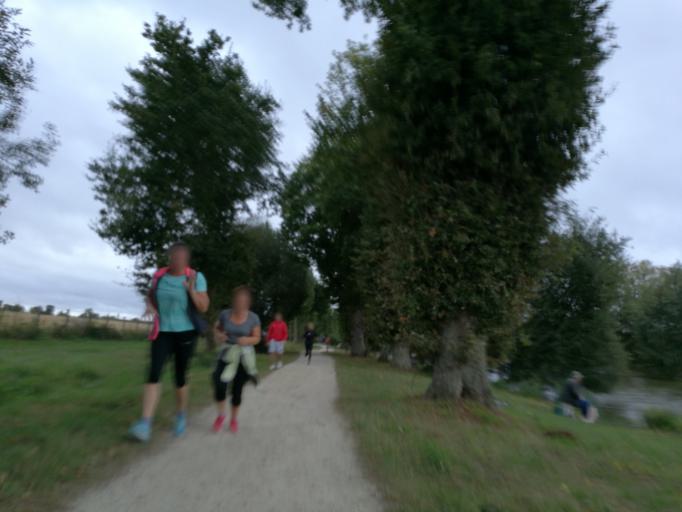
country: FR
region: Brittany
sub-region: Departement d'Ille-et-Vilaine
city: Bedee
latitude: 48.1677
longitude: -1.9535
